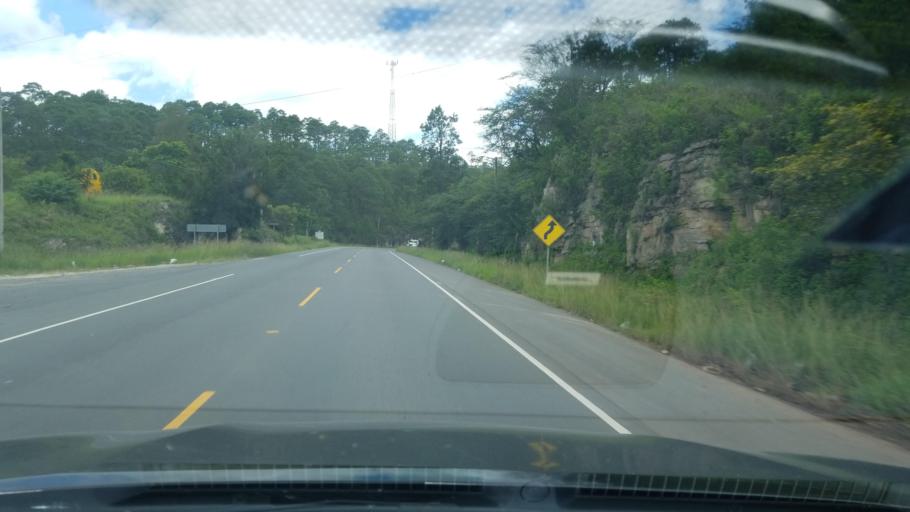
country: HN
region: Francisco Morazan
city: Talanga
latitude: 14.3537
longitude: -87.1555
